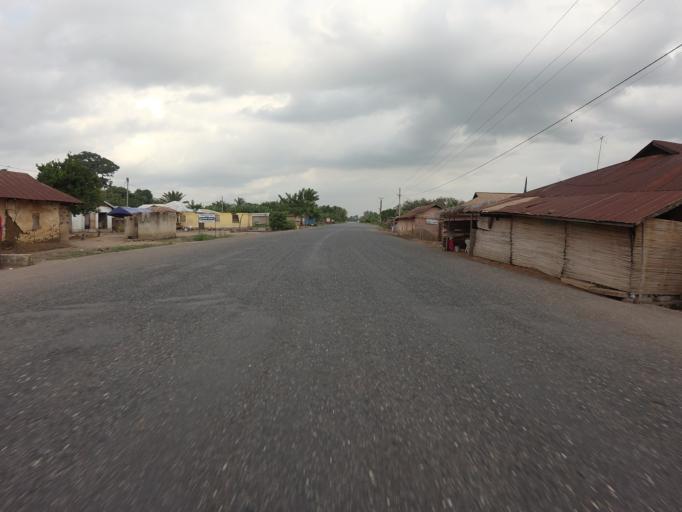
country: GH
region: Volta
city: Ho
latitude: 6.4874
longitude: 0.4893
